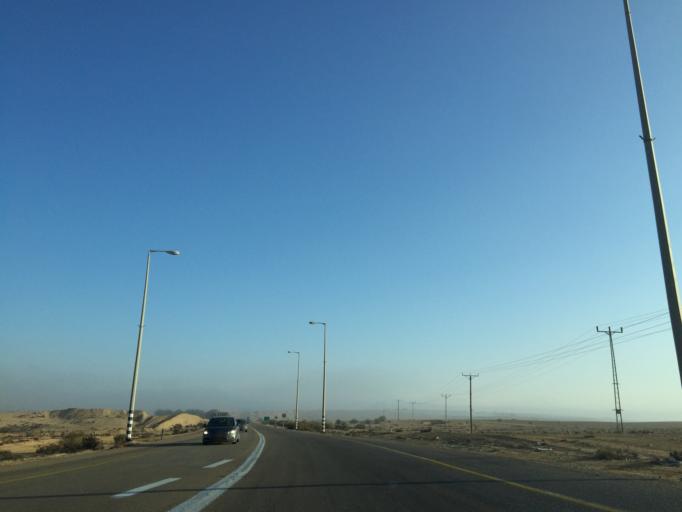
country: IL
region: Southern District
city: Yeroham
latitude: 30.9984
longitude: 34.9427
